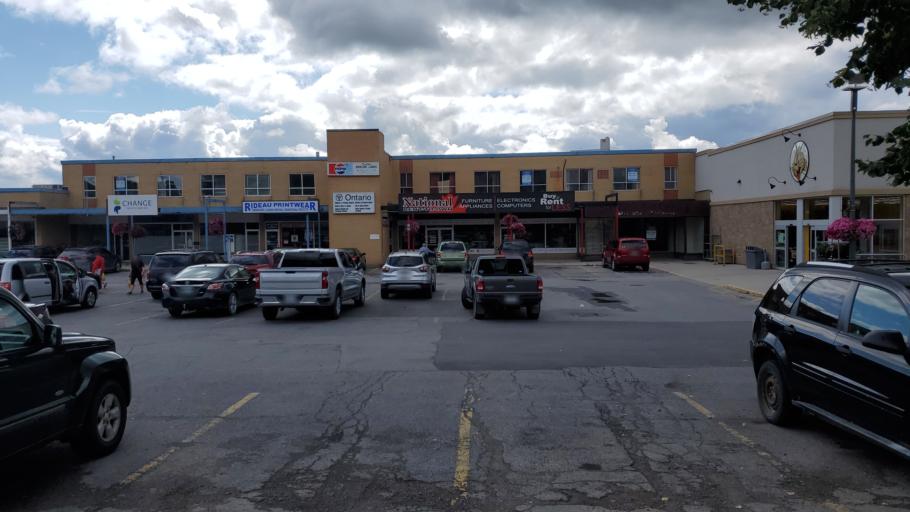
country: CA
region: Ontario
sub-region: Lanark County
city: Smiths Falls
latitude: 44.8988
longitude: -76.0185
